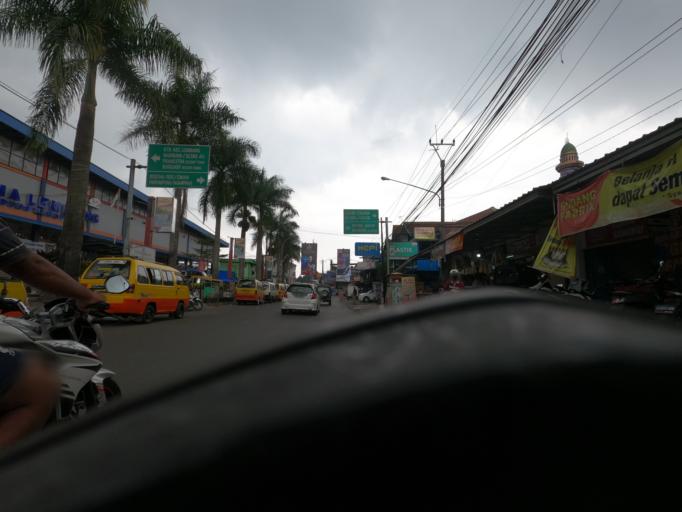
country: ID
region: West Java
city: Lembang
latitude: -6.8167
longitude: 107.6225
